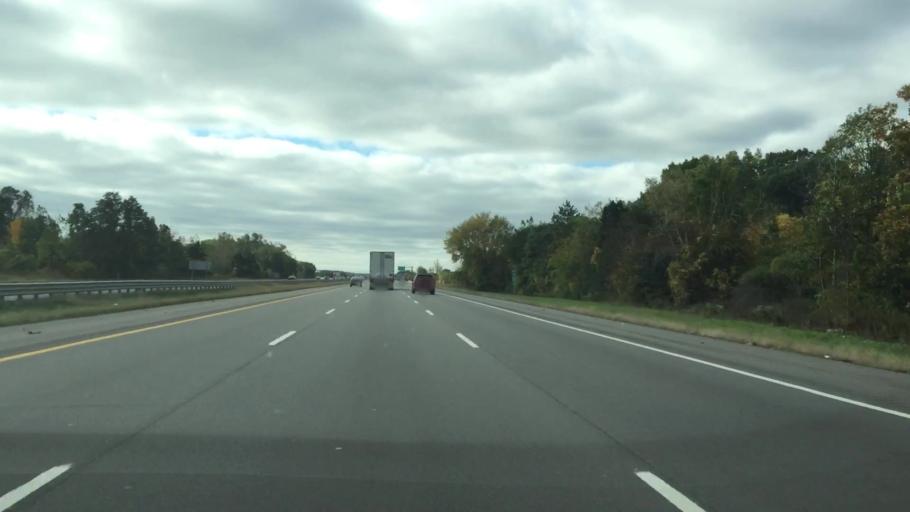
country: US
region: Michigan
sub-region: Macomb County
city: Mount Clemens
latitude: 42.6540
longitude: -82.8355
